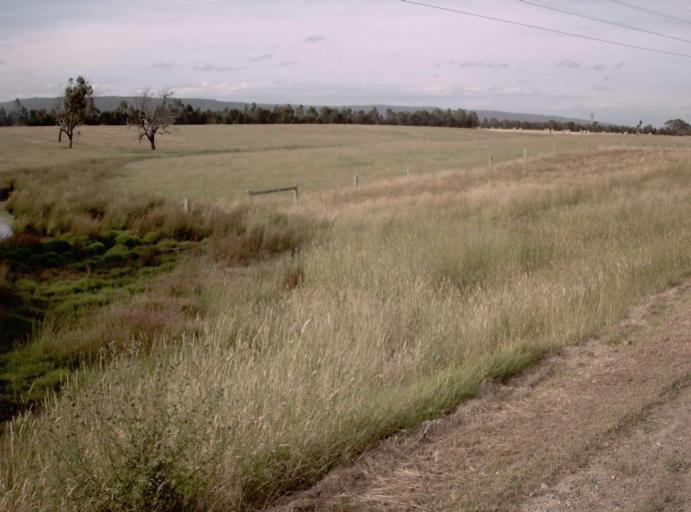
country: AU
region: Victoria
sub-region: Latrobe
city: Traralgon
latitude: -38.1133
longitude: 146.5828
